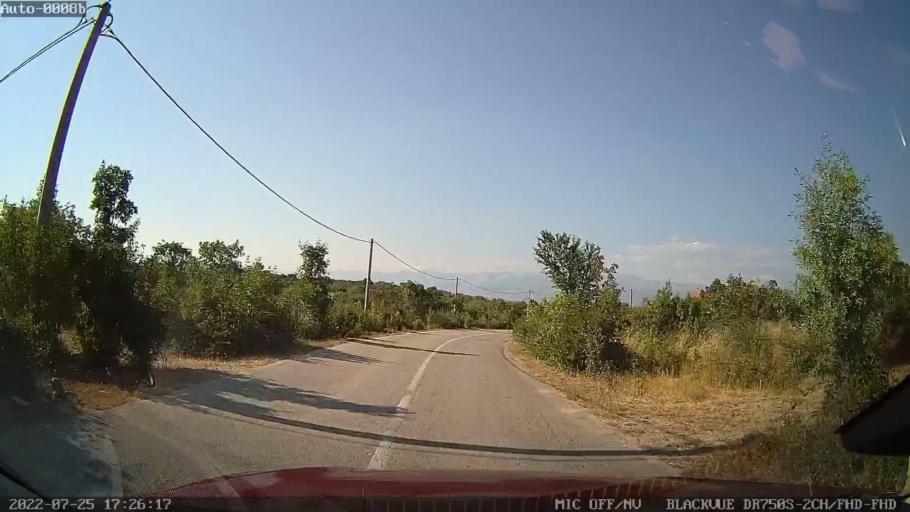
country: HR
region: Zadarska
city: Pridraga
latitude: 44.1326
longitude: 15.5002
